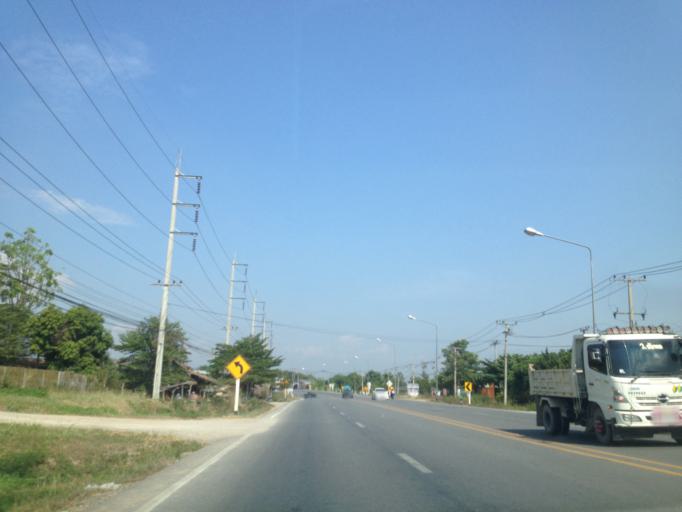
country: TH
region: Chiang Mai
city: Chom Thong
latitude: 18.3447
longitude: 98.6799
